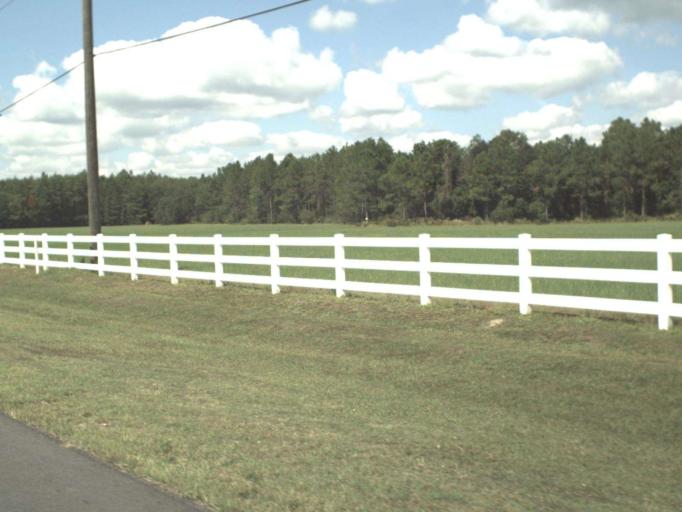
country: US
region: Florida
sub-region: Walton County
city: Freeport
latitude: 30.5077
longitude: -86.1637
